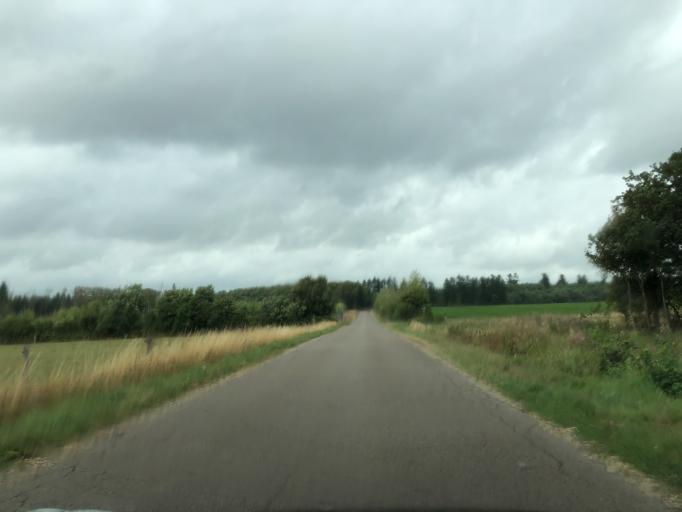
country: DK
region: Central Jutland
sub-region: Holstebro Kommune
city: Ulfborg
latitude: 56.1555
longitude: 8.4079
